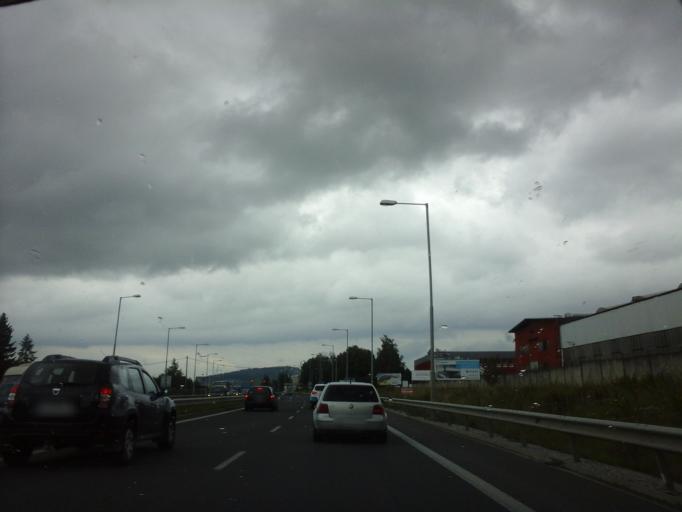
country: SK
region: Presovsky
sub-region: Okres Poprad
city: Poprad
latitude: 49.0647
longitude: 20.3201
